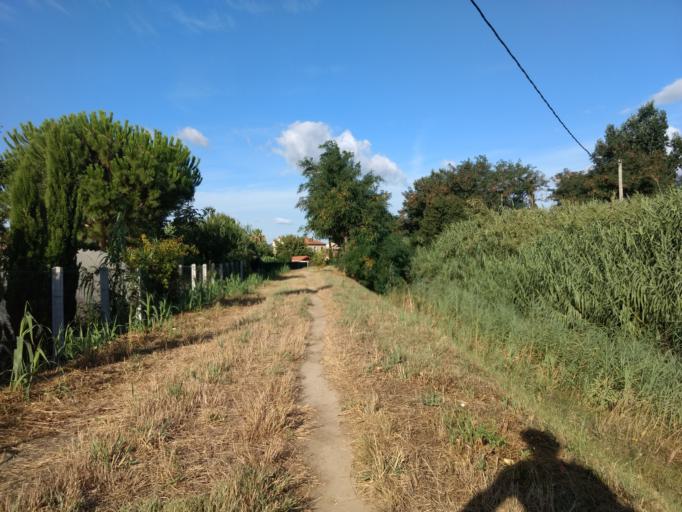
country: FR
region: Languedoc-Roussillon
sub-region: Departement des Pyrenees-Orientales
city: Saint-Laurent-de-la-Salanque
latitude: 42.7808
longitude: 2.9937
